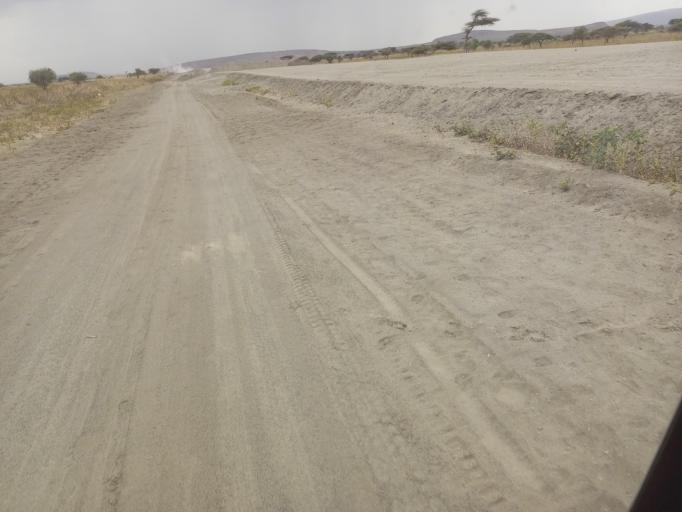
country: ET
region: Oromiya
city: Ziway
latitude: 7.8483
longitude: 38.6623
